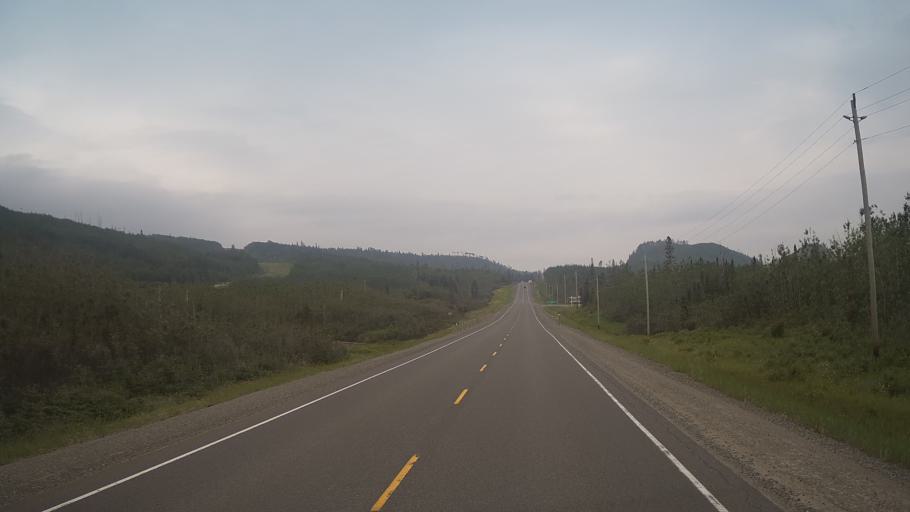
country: CA
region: Ontario
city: Greenstone
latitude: 49.4803
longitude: -88.0896
